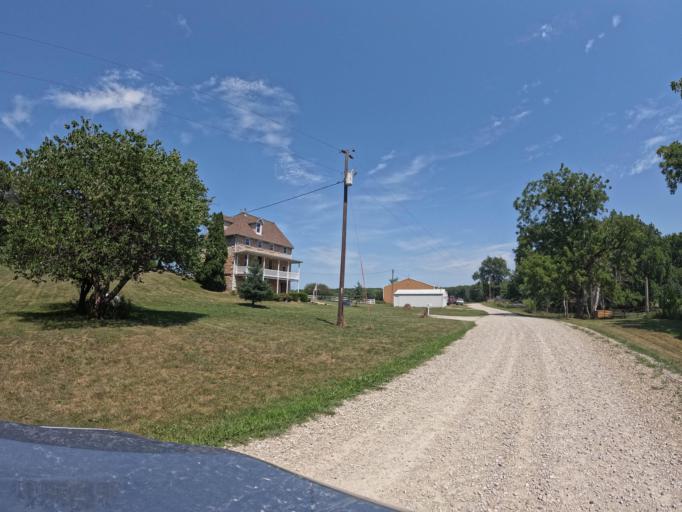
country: US
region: Iowa
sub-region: Henry County
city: Mount Pleasant
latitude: 40.8910
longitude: -91.6822
